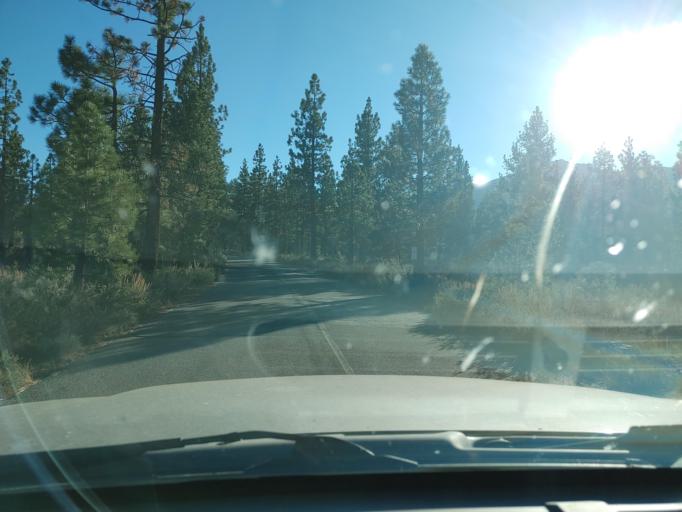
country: US
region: California
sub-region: El Dorado County
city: South Lake Tahoe
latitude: 38.9371
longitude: -120.0489
